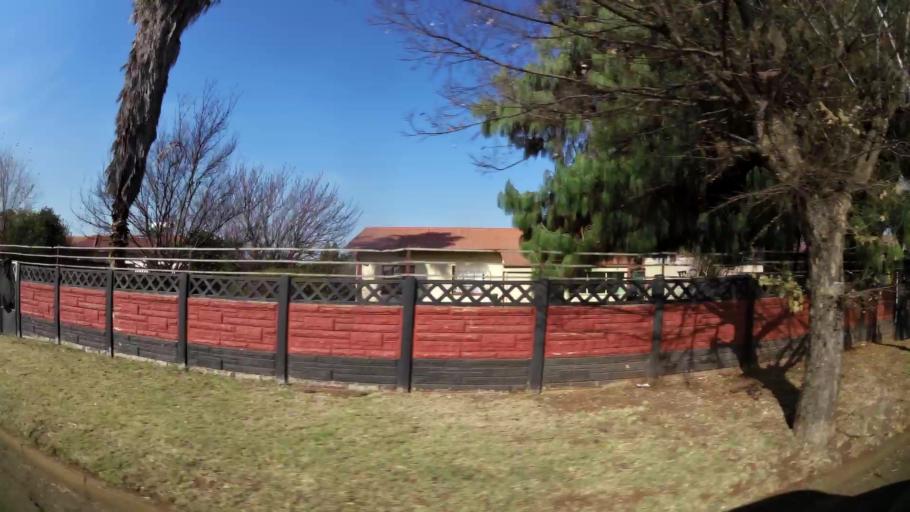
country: ZA
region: Gauteng
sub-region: West Rand District Municipality
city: Randfontein
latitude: -26.1840
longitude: 27.6914
